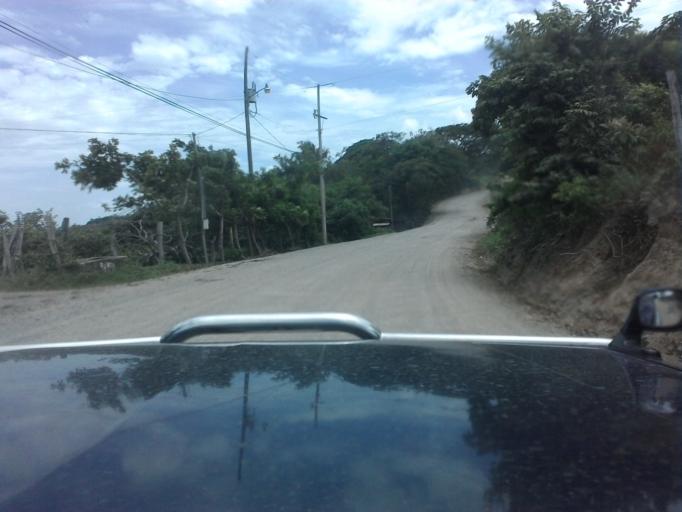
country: CR
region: Guanacaste
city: Juntas
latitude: 10.2317
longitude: -84.8509
